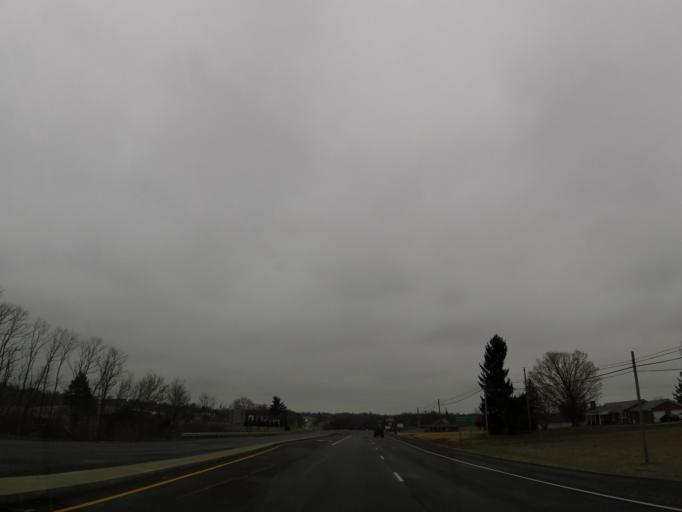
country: US
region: Kentucky
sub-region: Anderson County
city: Lawrenceburg
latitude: 37.9692
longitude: -84.8741
